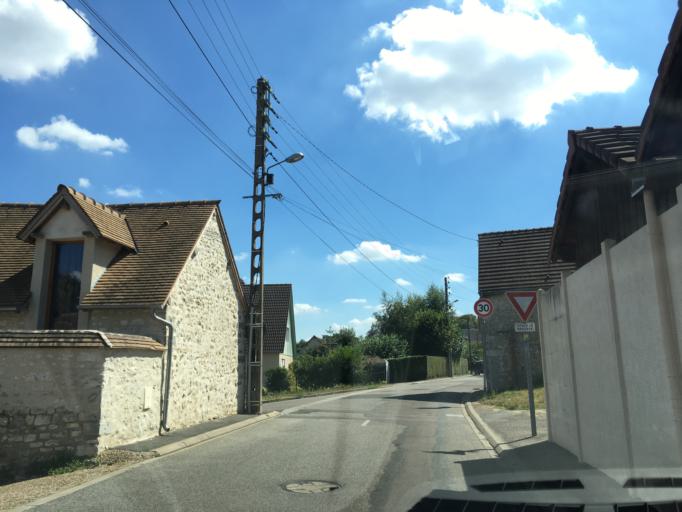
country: FR
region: Haute-Normandie
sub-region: Departement de l'Eure
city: Vernon
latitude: 49.0881
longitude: 1.4598
